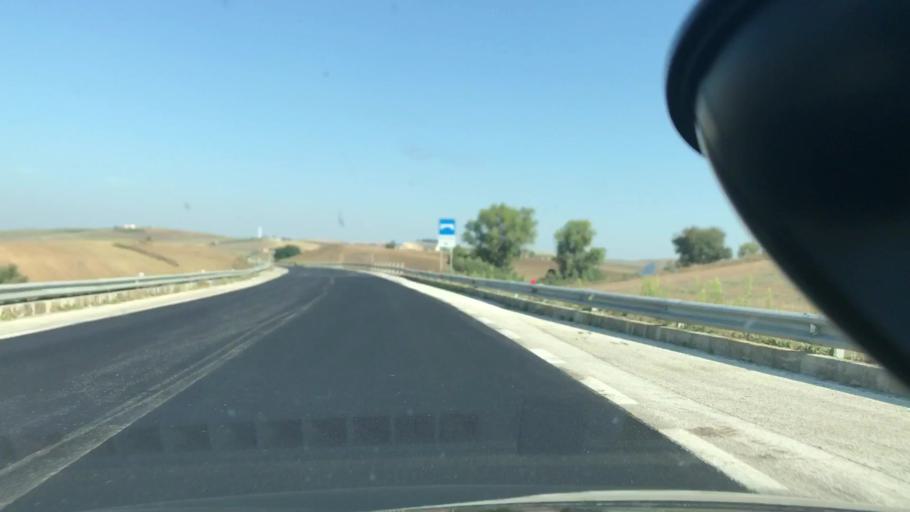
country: IT
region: Apulia
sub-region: Provincia di Barletta - Andria - Trani
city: Spinazzola
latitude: 40.9117
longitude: 16.1060
